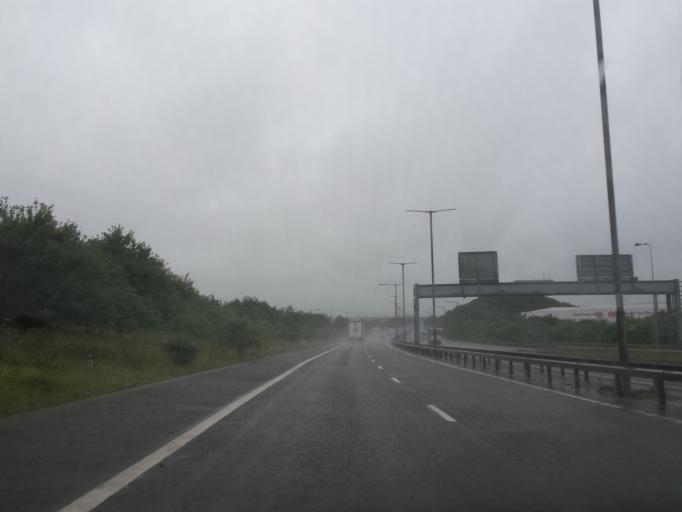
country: GB
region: England
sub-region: Warwickshire
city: Brandon
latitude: 52.4330
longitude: -1.4232
